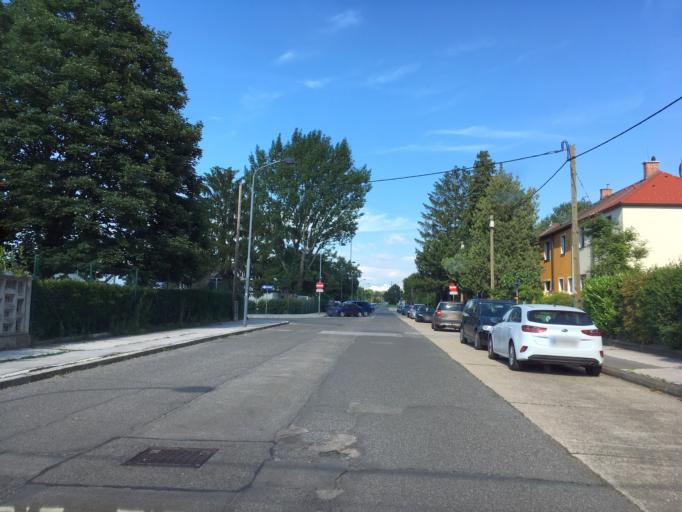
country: AT
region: Lower Austria
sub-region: Politischer Bezirk Korneuburg
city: Langenzersdorf
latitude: 48.2737
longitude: 16.3855
